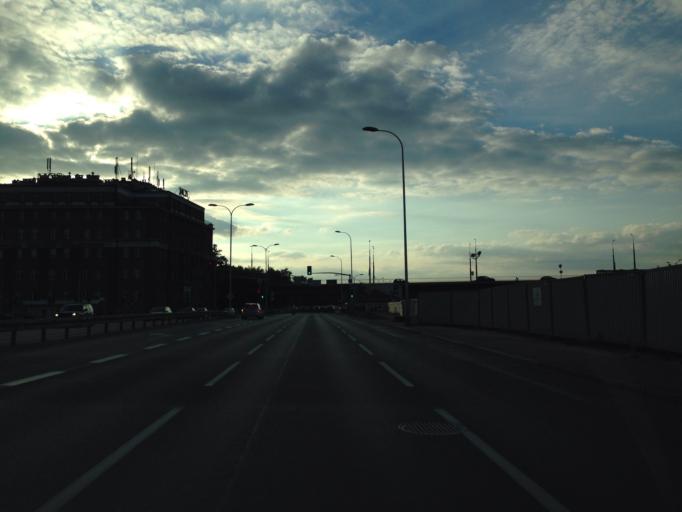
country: PL
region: Masovian Voivodeship
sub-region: Warszawa
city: Praga Polnoc
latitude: 52.2469
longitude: 21.0209
